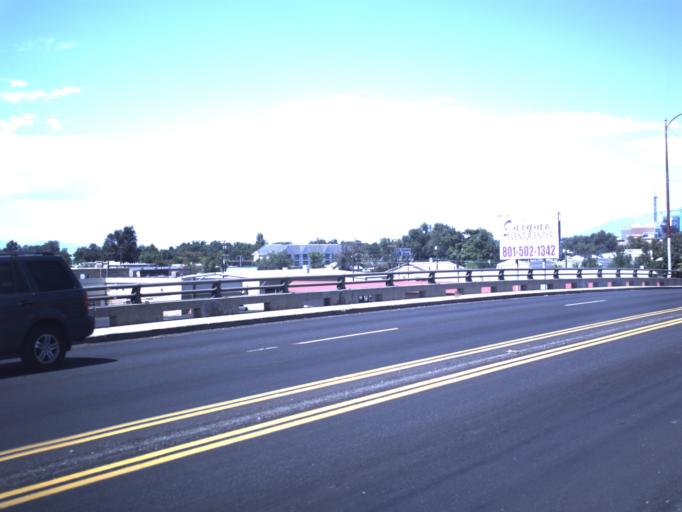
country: US
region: Utah
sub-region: Utah County
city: Provo
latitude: 40.2253
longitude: -111.6587
